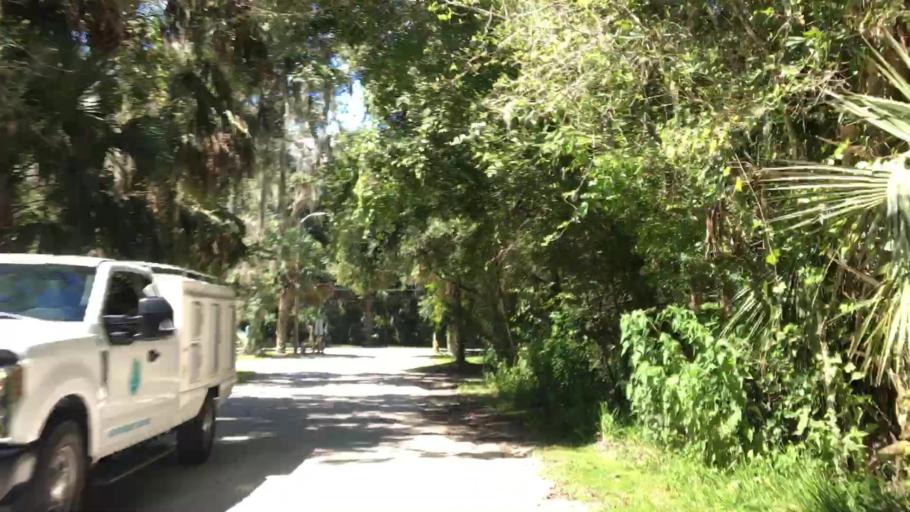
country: US
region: Florida
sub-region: Volusia County
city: Deltona
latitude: 28.8593
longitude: -81.2415
